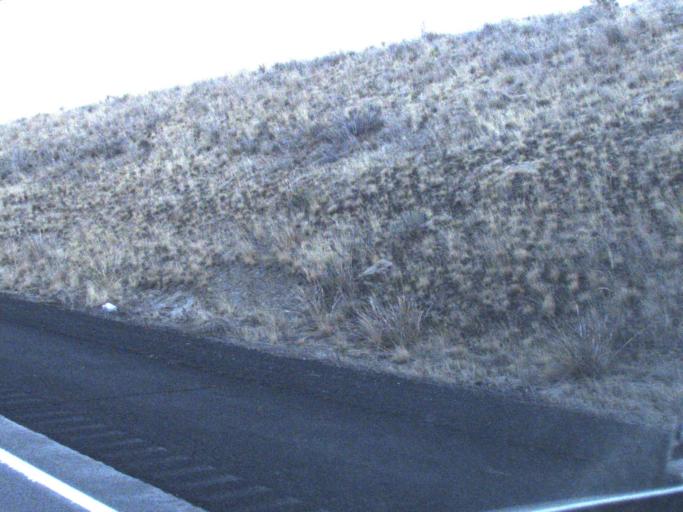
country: US
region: Washington
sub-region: Adams County
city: Ritzville
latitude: 46.9210
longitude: -118.5992
